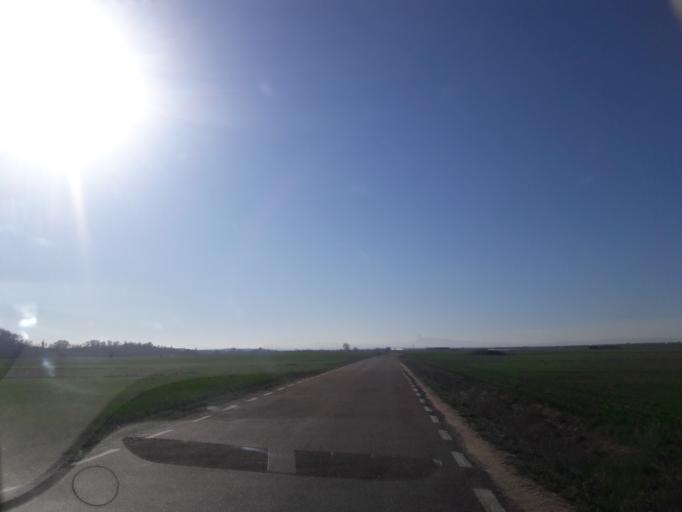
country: ES
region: Castille and Leon
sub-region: Provincia de Salamanca
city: Coca de Alba
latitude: 40.8672
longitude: -5.3733
